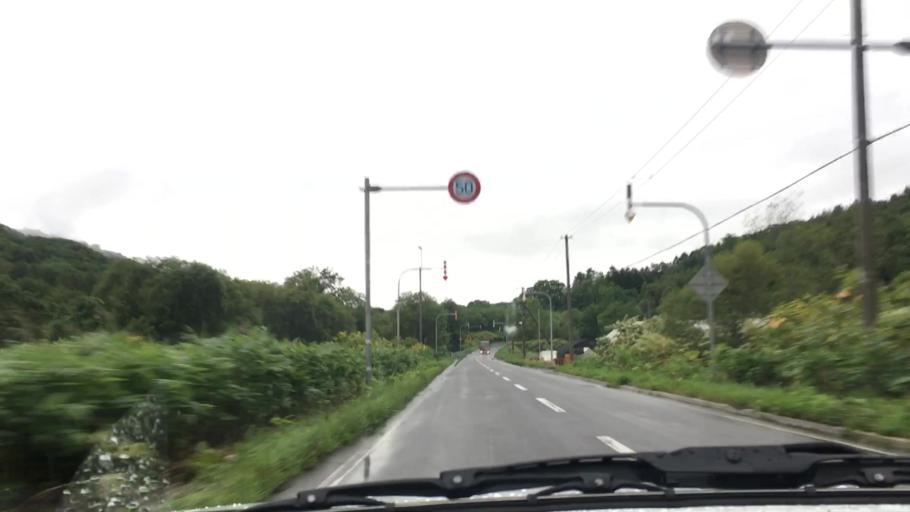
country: JP
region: Hokkaido
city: Niseko Town
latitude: 42.6583
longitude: 140.7449
